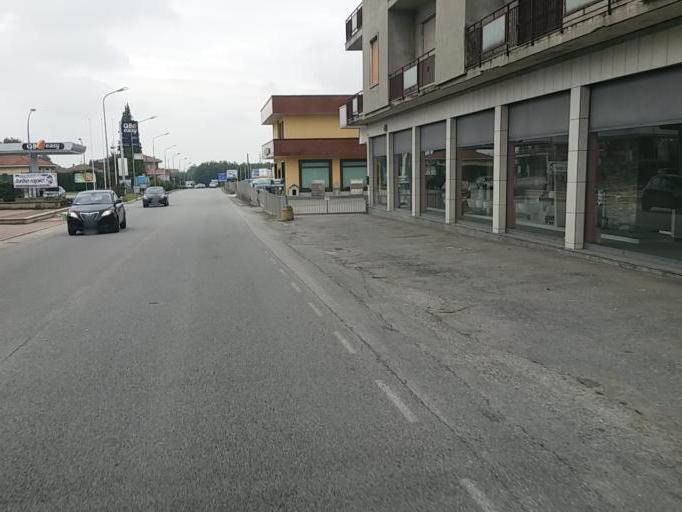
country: IT
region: Piedmont
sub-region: Provincia di Novara
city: Briga Novarese
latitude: 45.7277
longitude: 8.4445
